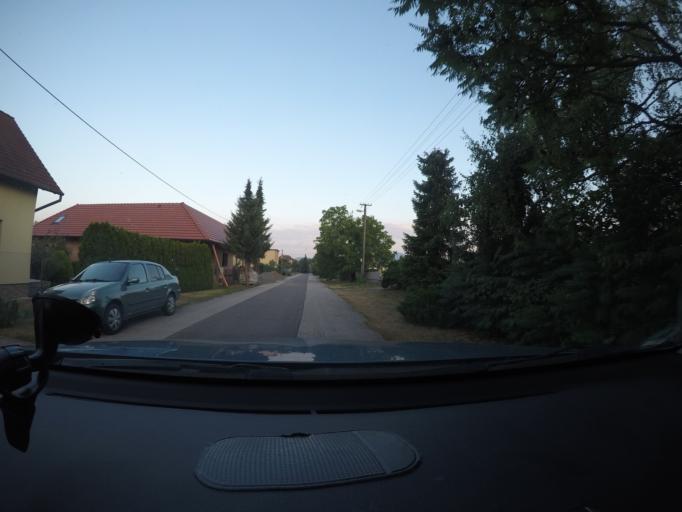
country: SK
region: Trenciansky
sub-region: Okres Trencin
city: Trencin
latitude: 48.8784
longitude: 17.9686
